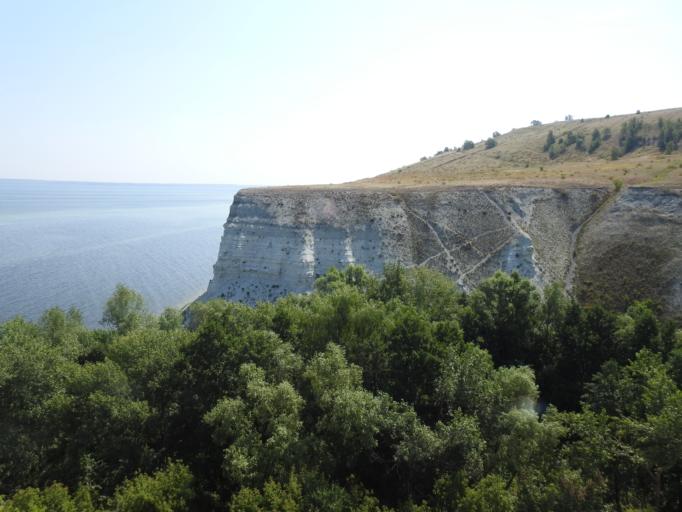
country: RU
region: Saratov
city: Kamenskiy
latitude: 50.6103
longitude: 45.6621
